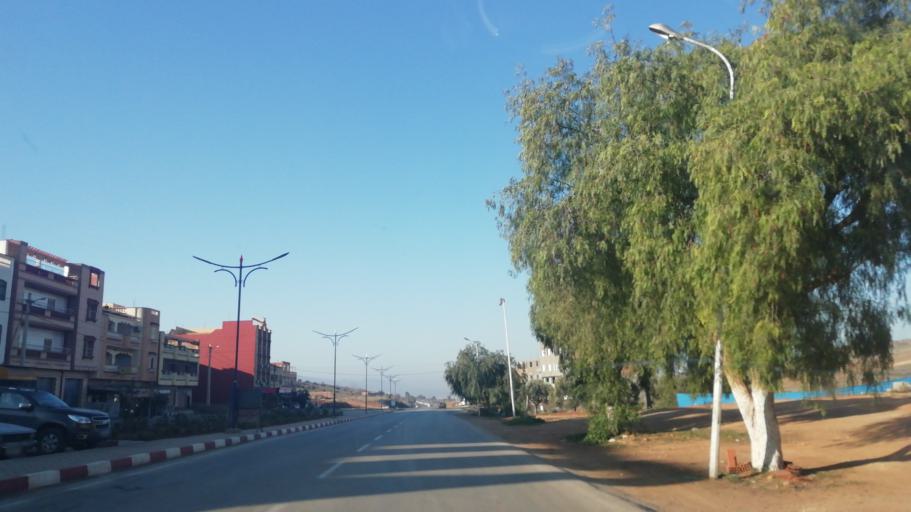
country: MA
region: Oriental
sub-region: Berkane-Taourirt
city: Ahfir
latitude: 34.9606
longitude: -2.0370
